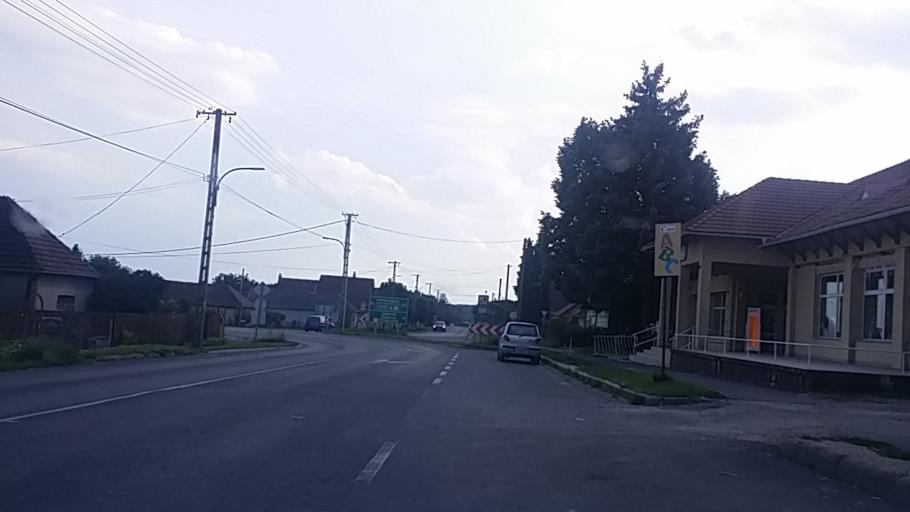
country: HU
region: Zala
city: Sarmellek
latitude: 46.7089
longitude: 17.1686
